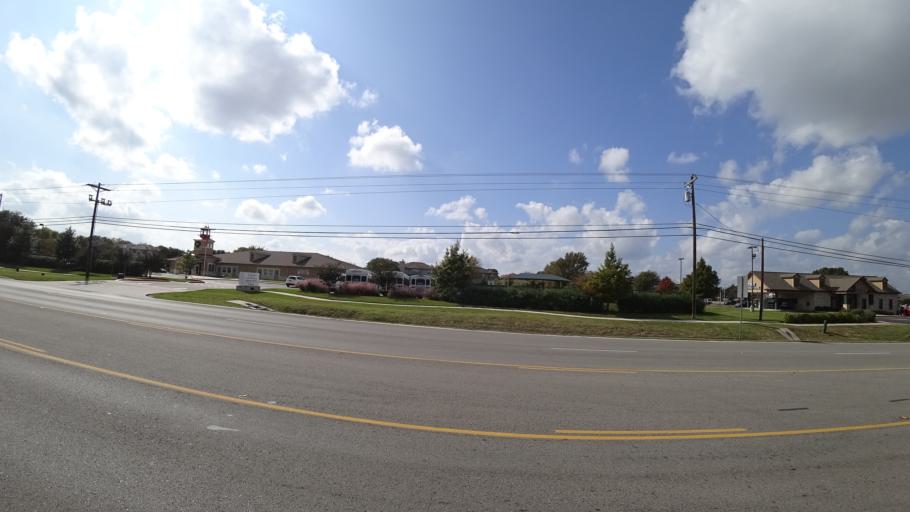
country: US
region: Texas
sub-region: Williamson County
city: Cedar Park
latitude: 30.5290
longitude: -97.8446
